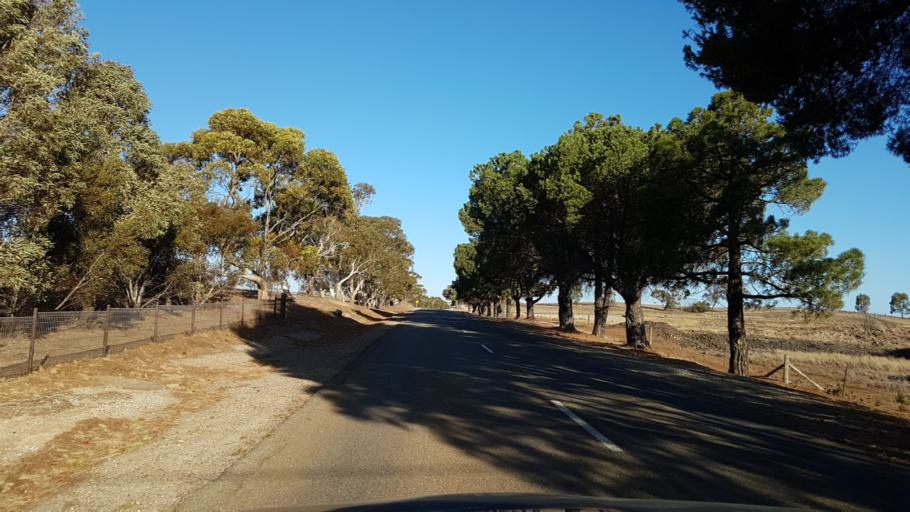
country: AU
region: South Australia
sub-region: Clare and Gilbert Valleys
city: Clare
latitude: -33.6731
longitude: 138.9368
